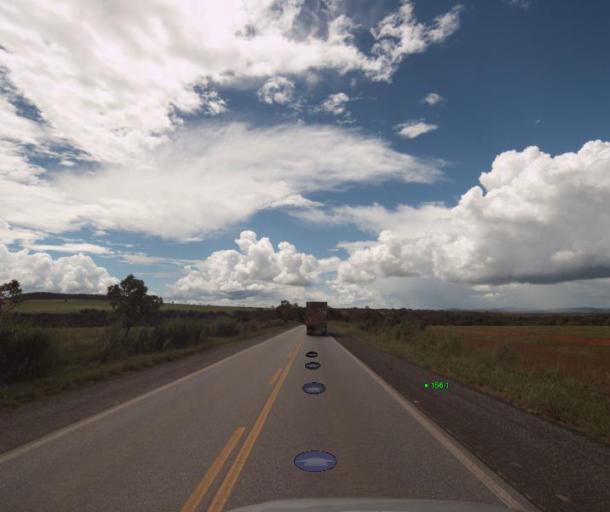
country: BR
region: Goias
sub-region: Uruacu
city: Uruacu
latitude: -14.1390
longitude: -49.1145
